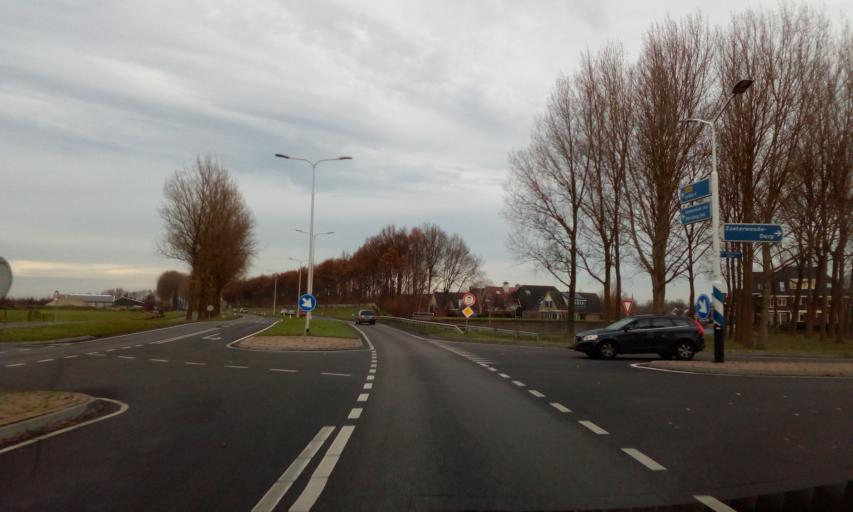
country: NL
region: South Holland
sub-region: Gemeente Leiden
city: Leiden
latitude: 52.1127
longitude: 4.4956
